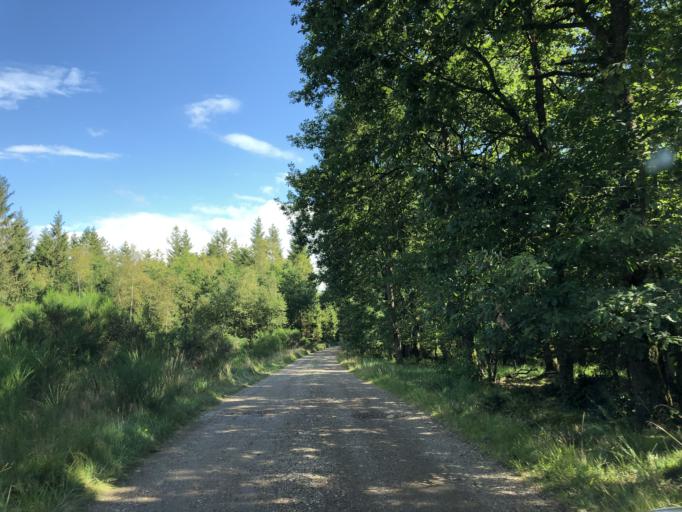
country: DK
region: Central Jutland
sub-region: Holstebro Kommune
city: Ulfborg
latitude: 56.2514
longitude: 8.4697
